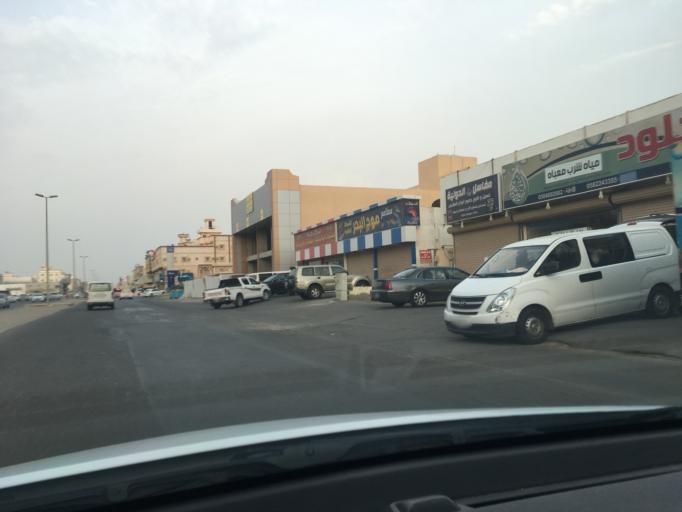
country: SA
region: Makkah
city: Jeddah
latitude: 21.7593
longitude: 39.1921
